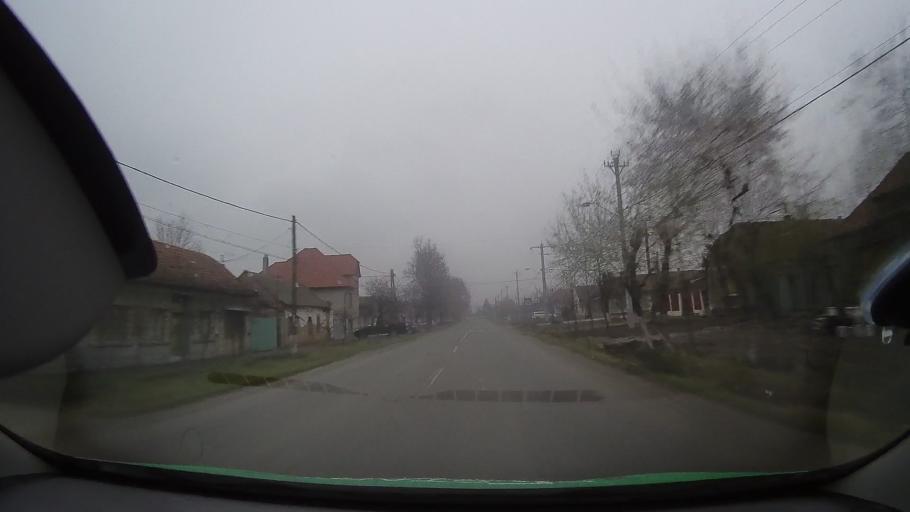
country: RO
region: Bihor
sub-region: Municipiul Salonta
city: Salonta
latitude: 46.8004
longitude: 21.6489
